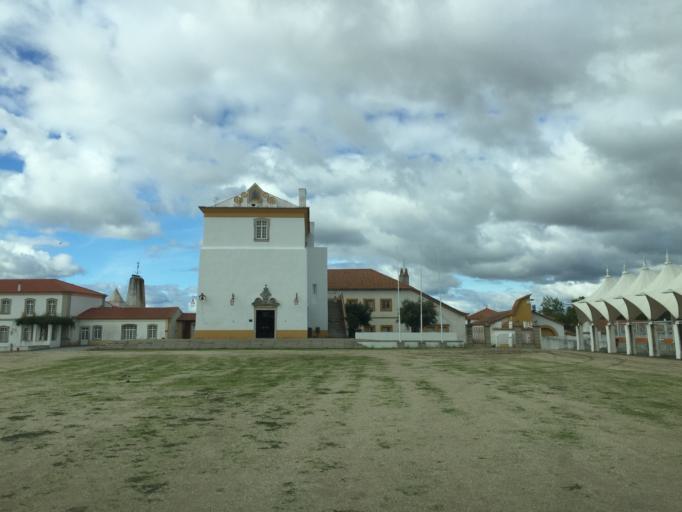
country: PT
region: Portalegre
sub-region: Alter do Chao
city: Alter do Chao
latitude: 39.2220
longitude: -7.6861
